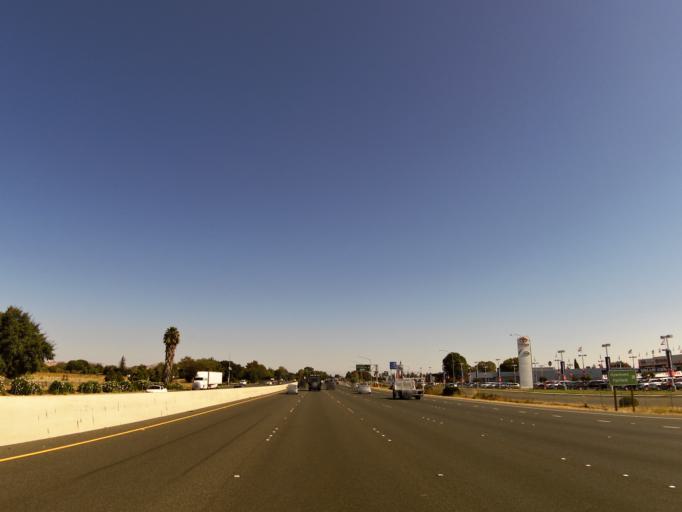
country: US
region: California
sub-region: Solano County
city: Suisun
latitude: 38.2443
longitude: -122.0821
